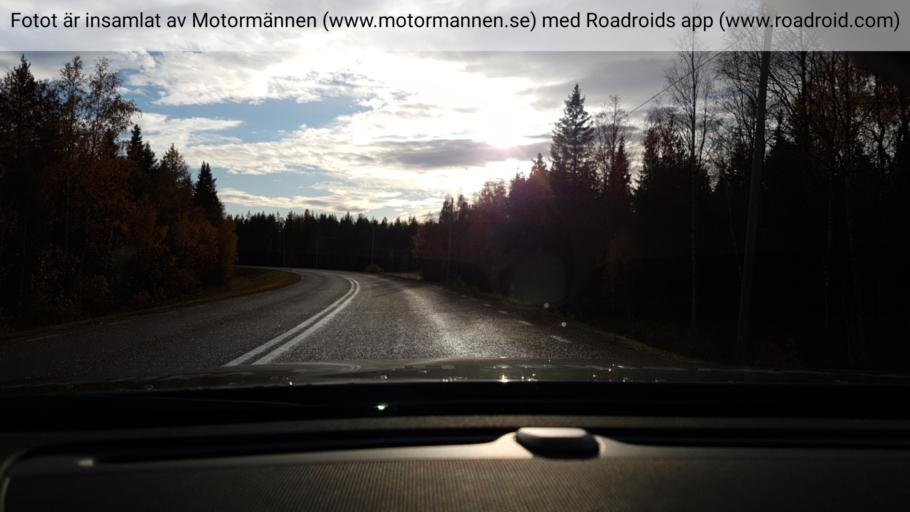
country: SE
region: Norrbotten
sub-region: Pajala Kommun
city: Pajala
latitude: 67.1653
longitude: 22.6381
